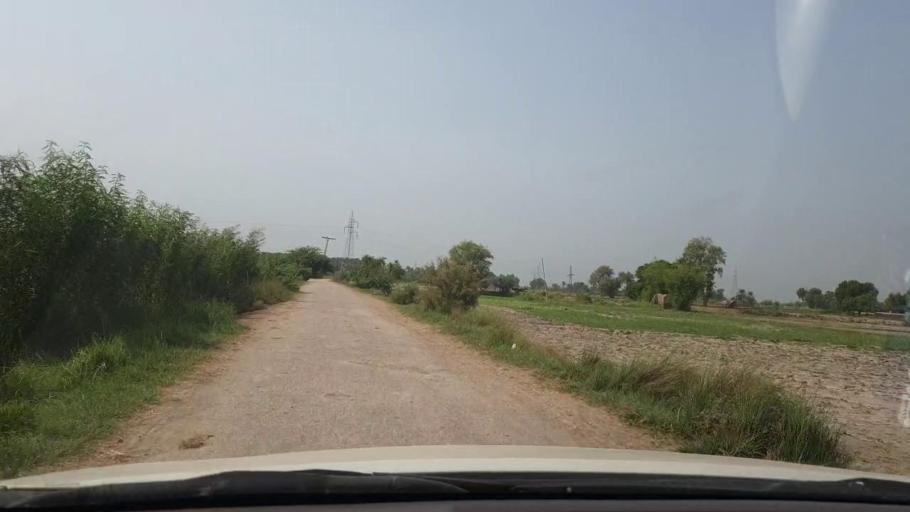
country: PK
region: Sindh
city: Shikarpur
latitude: 27.9774
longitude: 68.6737
